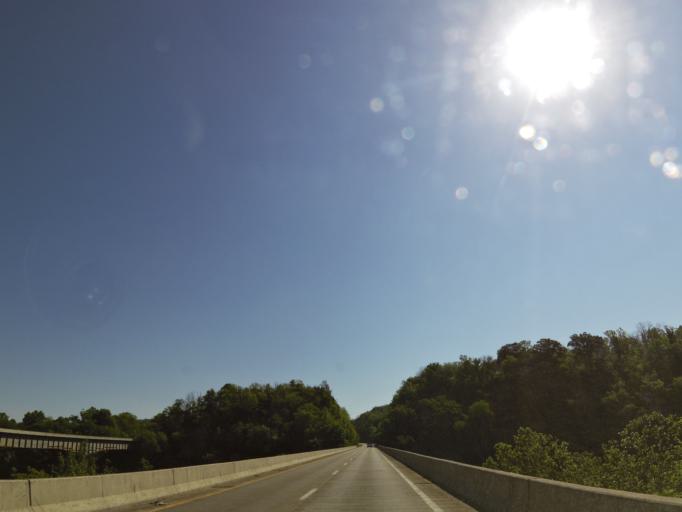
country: US
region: Kentucky
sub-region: Franklin County
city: Frankfort
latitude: 38.1605
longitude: -84.8531
